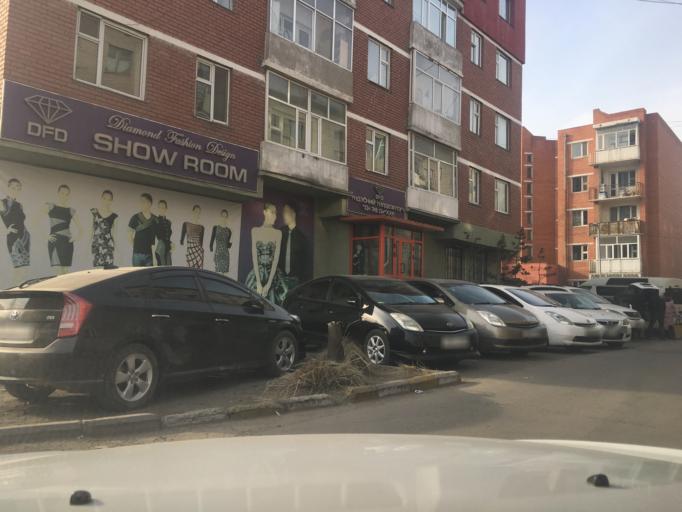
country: MN
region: Ulaanbaatar
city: Ulaanbaatar
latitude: 47.9105
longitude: 106.8830
